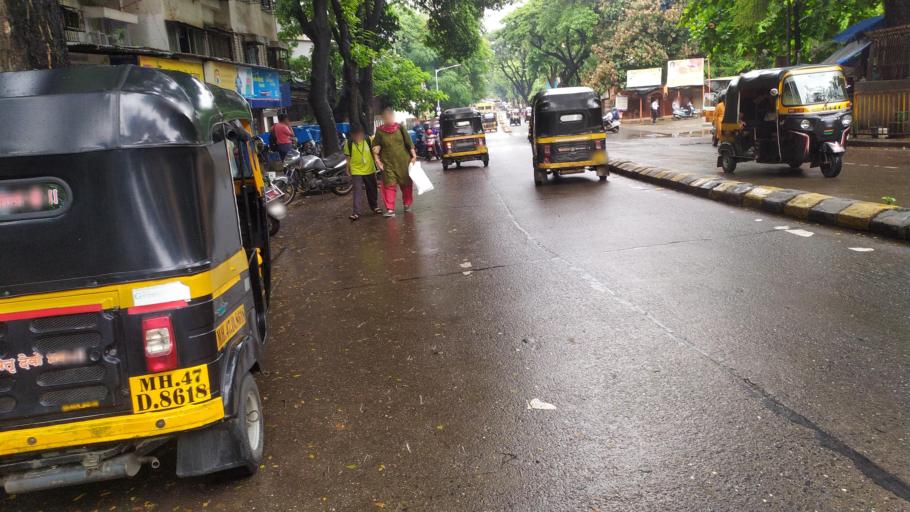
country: IN
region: Maharashtra
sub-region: Mumbai Suburban
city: Borivli
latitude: 19.2420
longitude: 72.8544
